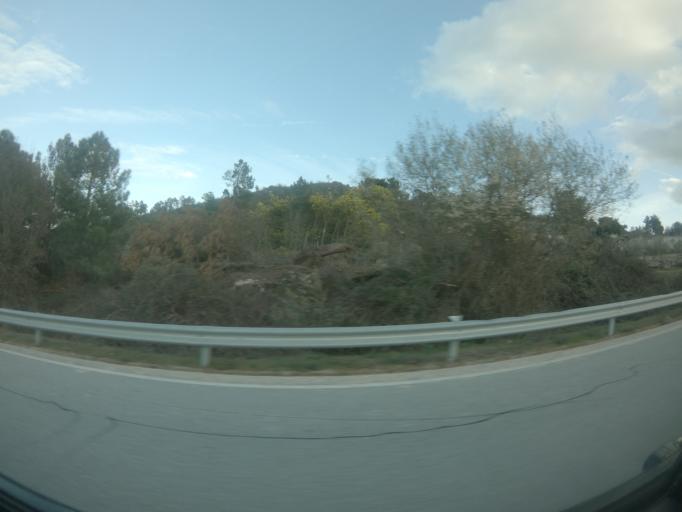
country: PT
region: Braganca
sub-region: Carrazeda de Ansiaes
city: Carrazeda de Anciaes
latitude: 41.2681
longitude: -7.3222
